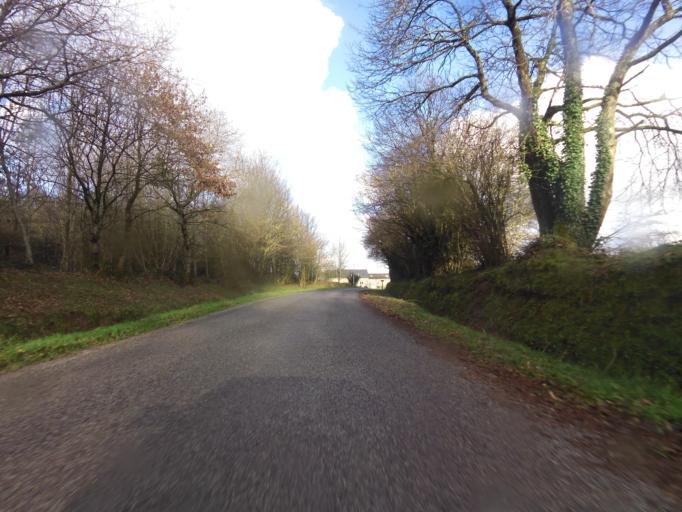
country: FR
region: Brittany
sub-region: Departement des Cotes-d'Armor
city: Rostrenen
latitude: 48.1784
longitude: -3.2858
